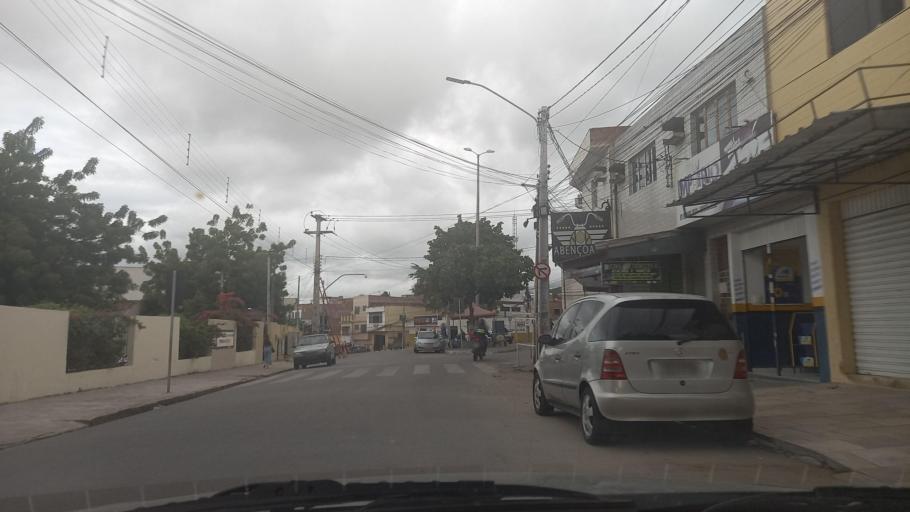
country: BR
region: Pernambuco
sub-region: Caruaru
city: Caruaru
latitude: -8.2928
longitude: -35.9699
